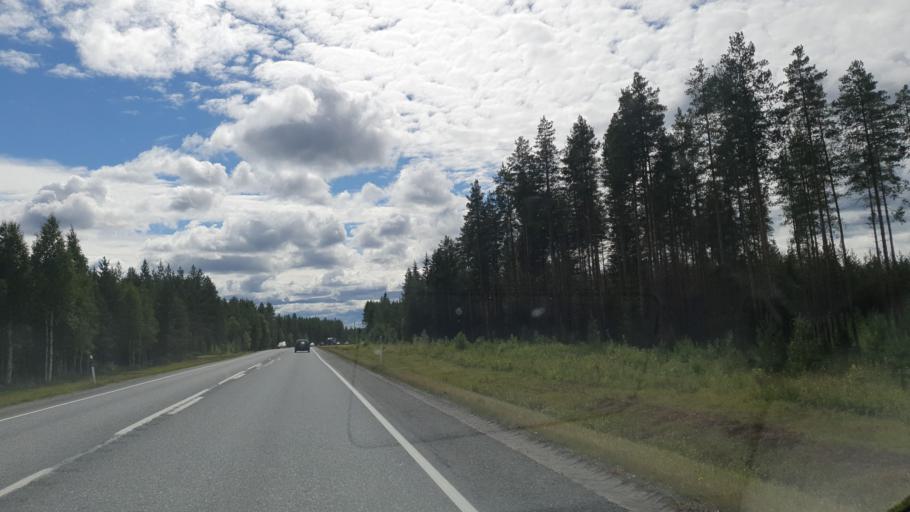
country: FI
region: Kainuu
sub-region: Kajaani
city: Kajaani
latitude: 64.1529
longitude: 27.5134
